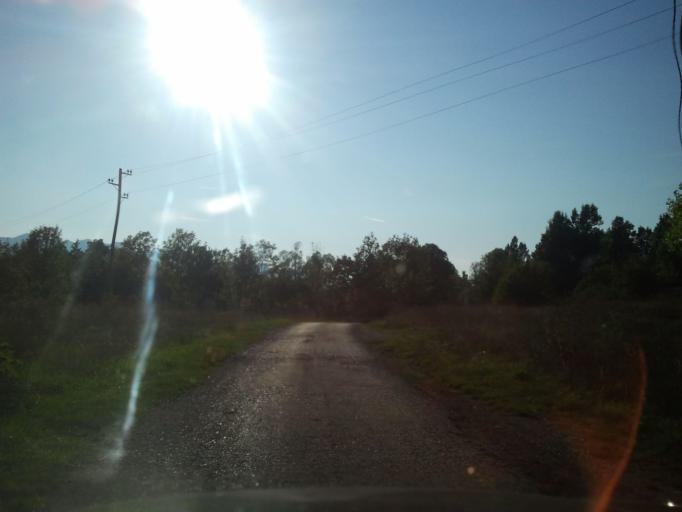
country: HR
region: Zadarska
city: Gracac
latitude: 44.3886
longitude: 15.6895
